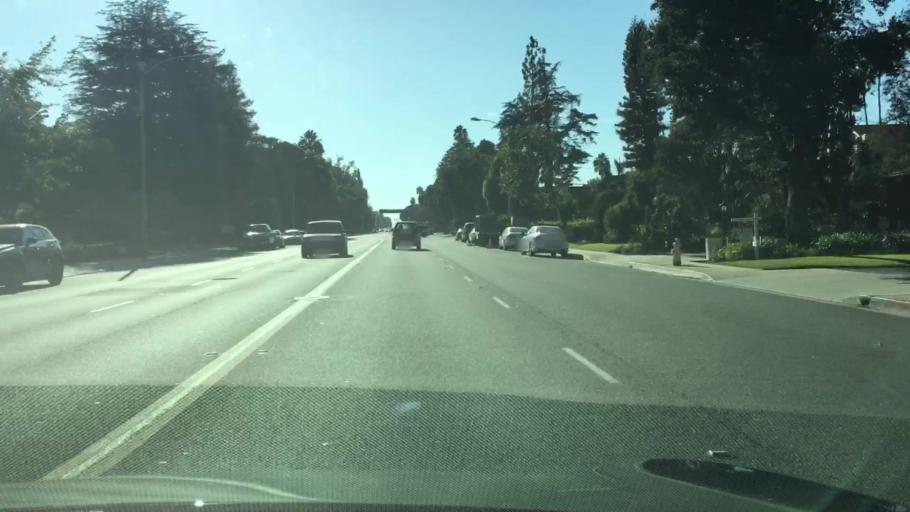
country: US
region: California
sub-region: Los Angeles County
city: Arcadia
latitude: 34.1271
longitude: -118.0482
